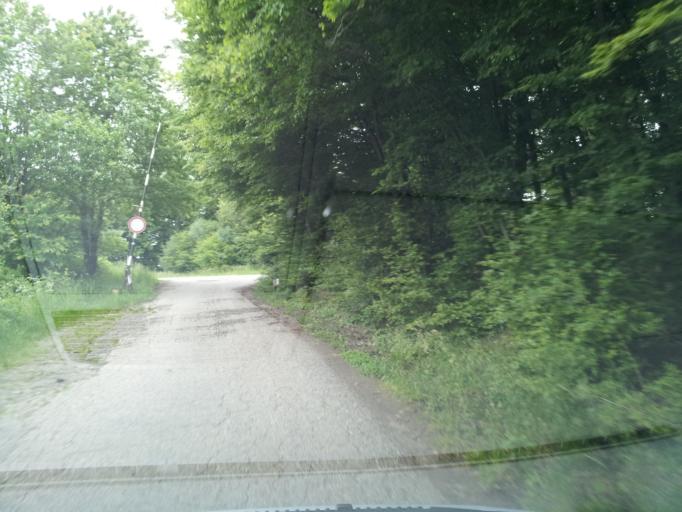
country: HU
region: Komarom-Esztergom
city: Kesztolc
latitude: 47.7364
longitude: 18.8470
